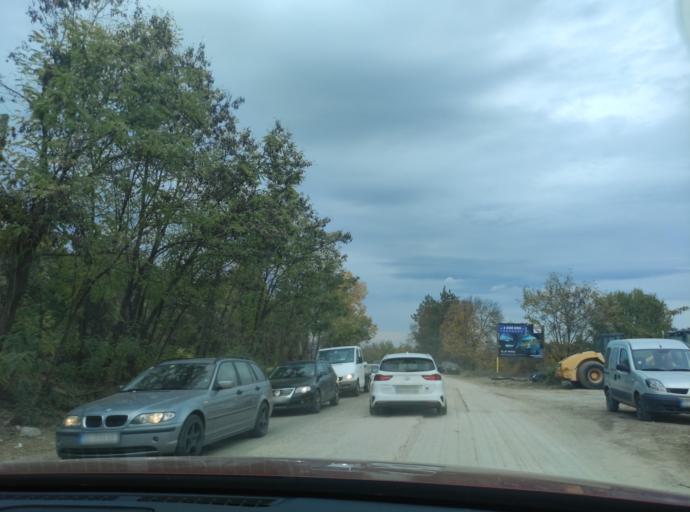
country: BG
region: Montana
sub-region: Obshtina Montana
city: Montana
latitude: 43.3852
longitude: 23.2435
